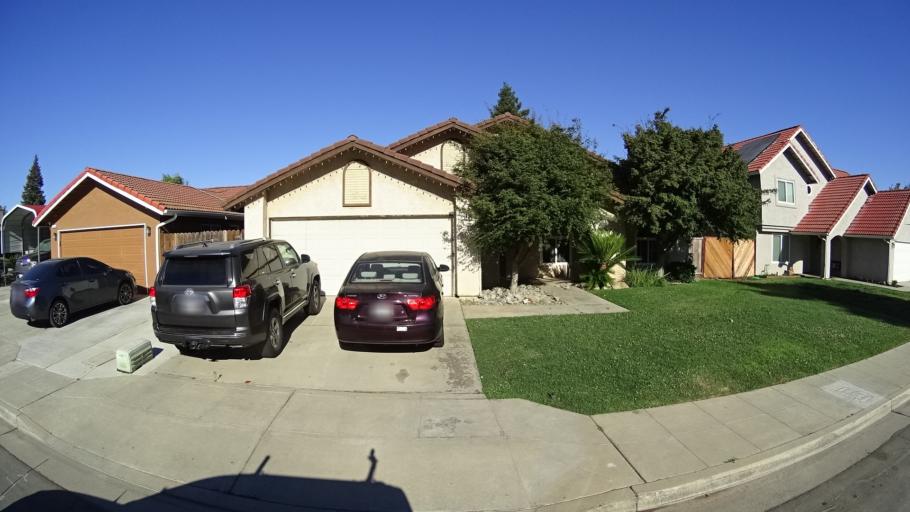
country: US
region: California
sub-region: Fresno County
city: West Park
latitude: 36.7841
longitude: -119.8647
